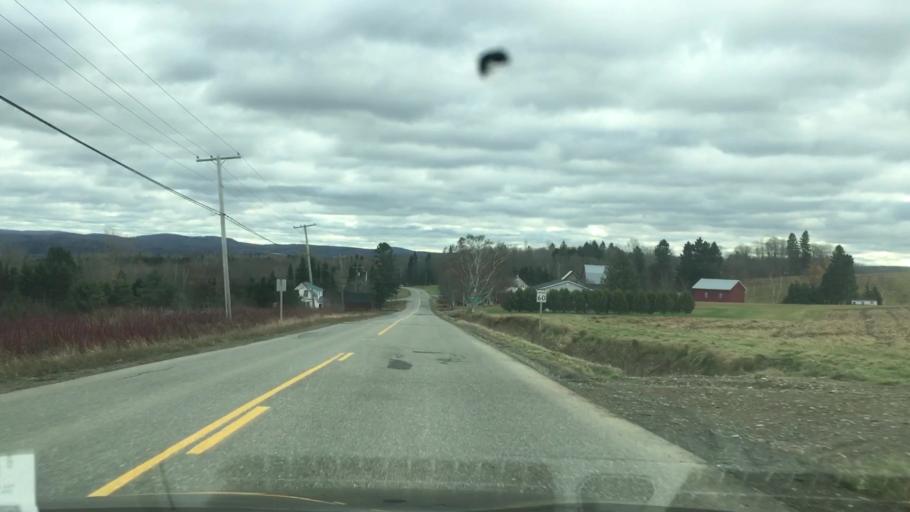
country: US
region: Maine
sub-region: Aroostook County
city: Fort Fairfield
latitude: 46.7533
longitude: -67.7589
